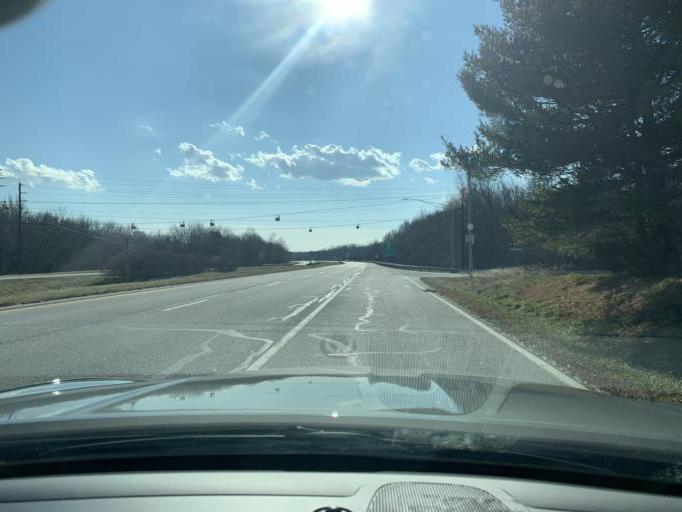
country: US
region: Maryland
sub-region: Queen Anne's County
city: Kingstown
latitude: 39.2747
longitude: -75.8615
